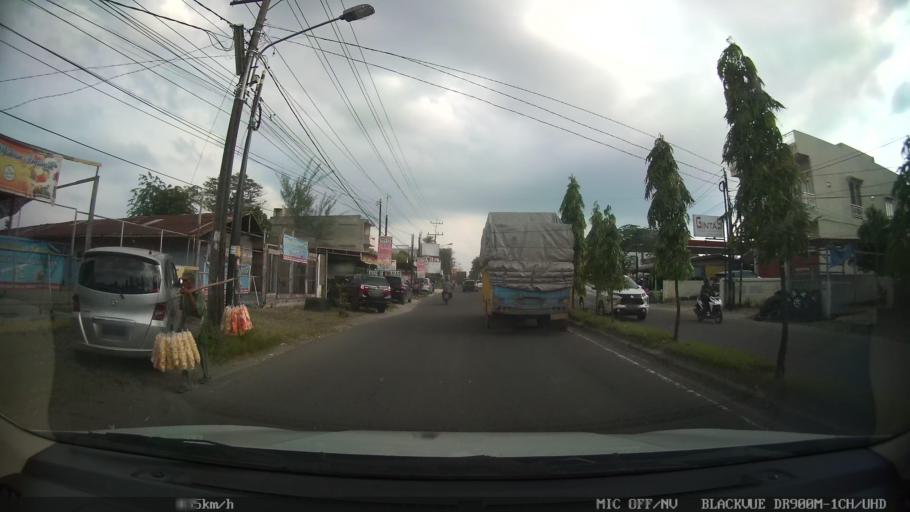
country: ID
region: North Sumatra
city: Sunggal
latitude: 3.5388
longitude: 98.6224
